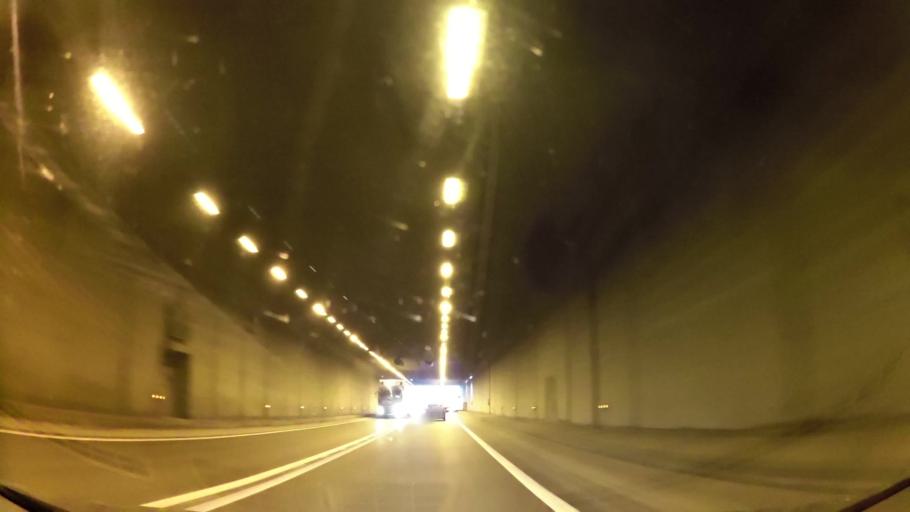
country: RS
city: Ostruznica
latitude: 44.7292
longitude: 20.3464
